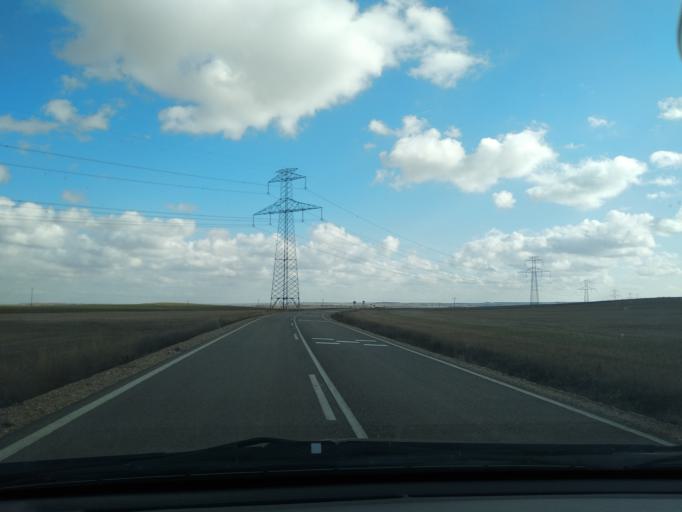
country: ES
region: Castille and Leon
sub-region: Provincia de Valladolid
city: Berrueces
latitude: 41.9484
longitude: -5.0709
